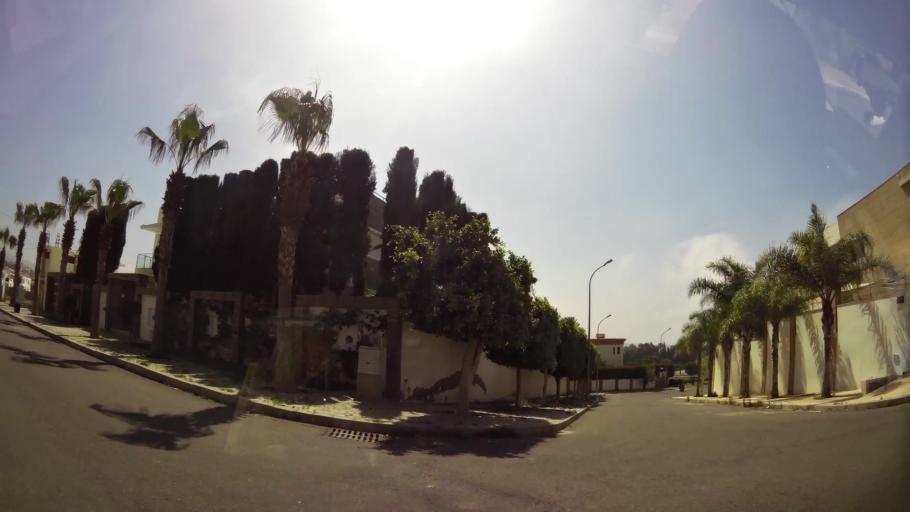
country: MA
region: Souss-Massa-Draa
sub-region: Agadir-Ida-ou-Tnan
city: Agadir
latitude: 30.4396
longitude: -9.5957
